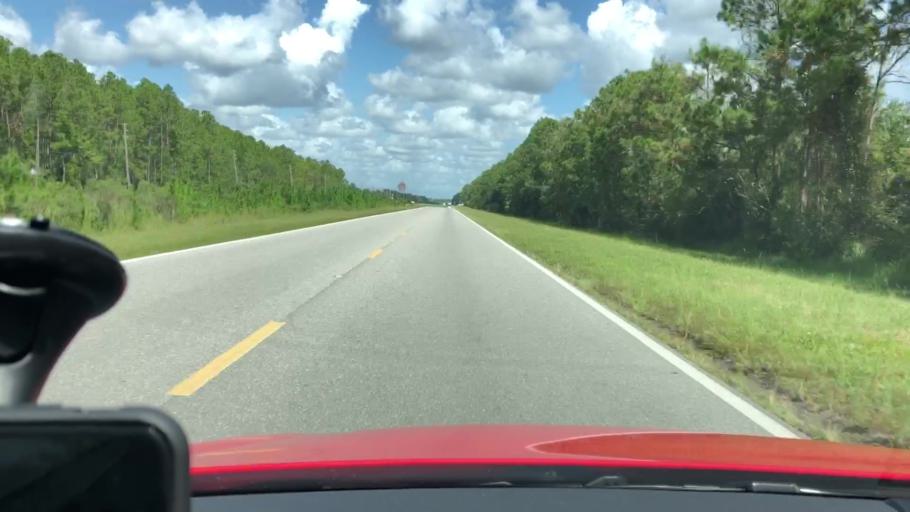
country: US
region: Florida
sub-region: Volusia County
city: Daytona Beach
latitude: 29.1848
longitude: -81.1197
